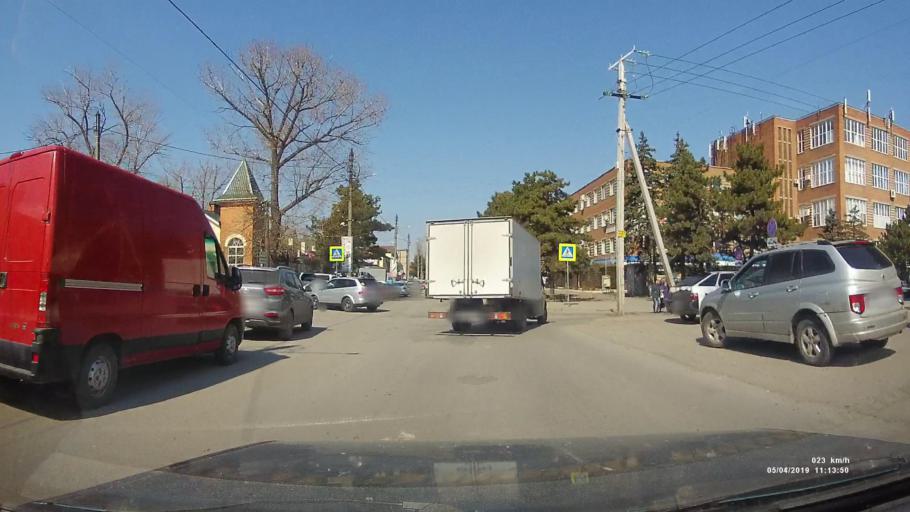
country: RU
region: Rostov
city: Azov
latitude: 47.1036
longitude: 39.4292
